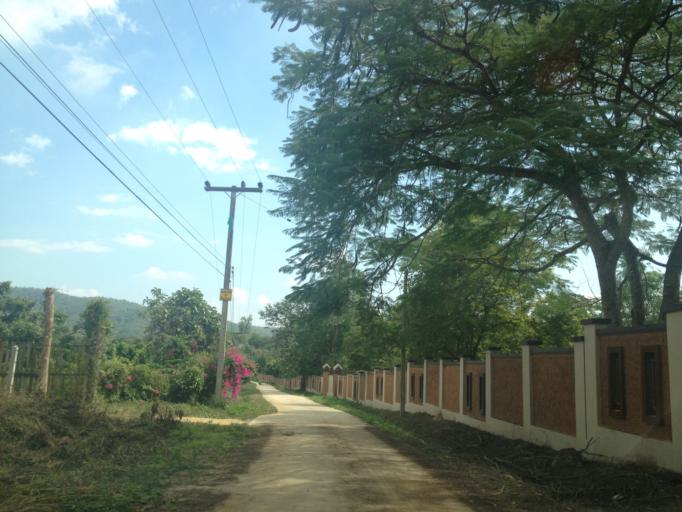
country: TH
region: Chiang Mai
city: Hang Dong
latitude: 18.7261
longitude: 98.8756
